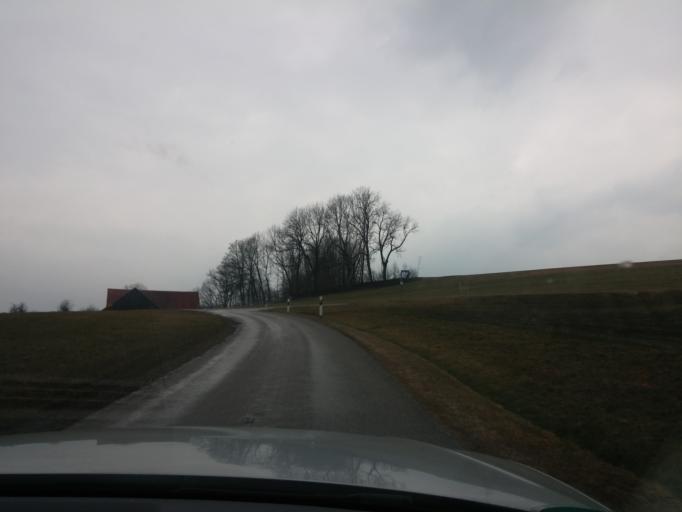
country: DE
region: Baden-Wuerttemberg
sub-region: Tuebingen Region
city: Leutkirch im Allgau
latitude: 47.8389
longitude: 10.0598
